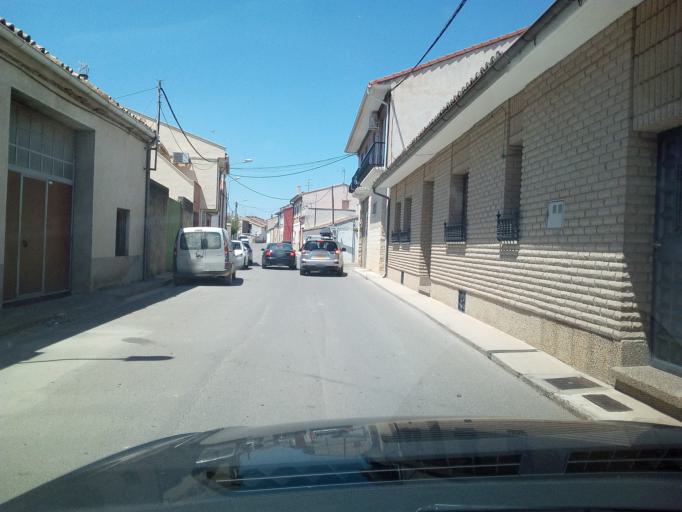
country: ES
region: Navarre
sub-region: Provincia de Navarra
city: Arguedas
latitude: 42.1742
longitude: -1.5938
